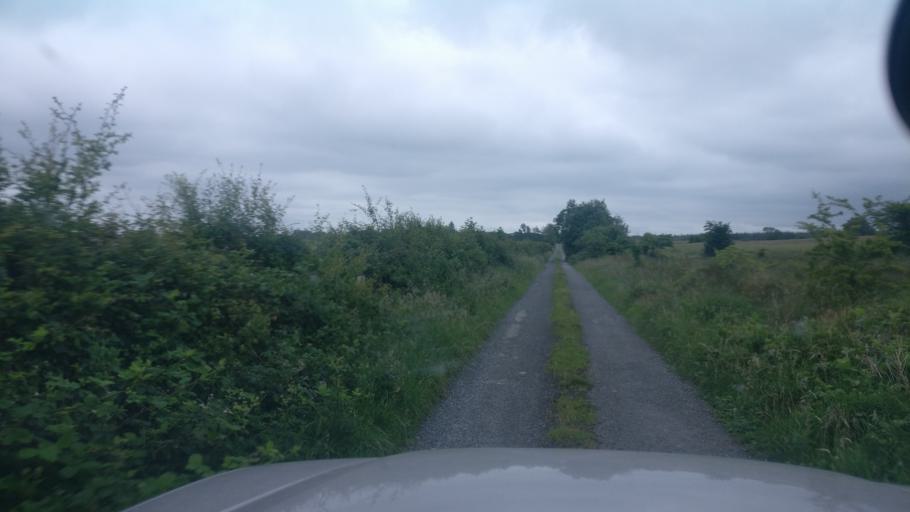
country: IE
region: Connaught
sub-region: County Galway
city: Ballinasloe
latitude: 53.3004
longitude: -8.3621
